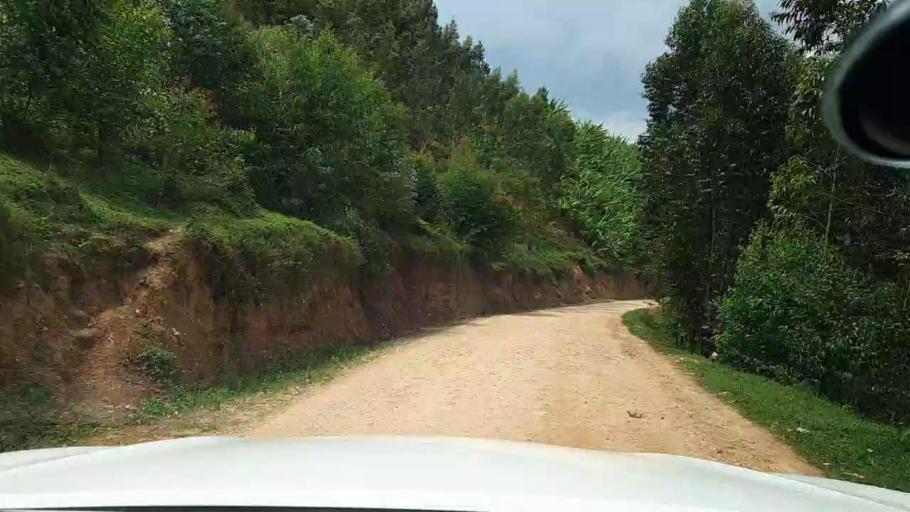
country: RW
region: Western Province
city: Kibuye
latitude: -2.1231
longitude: 29.4251
